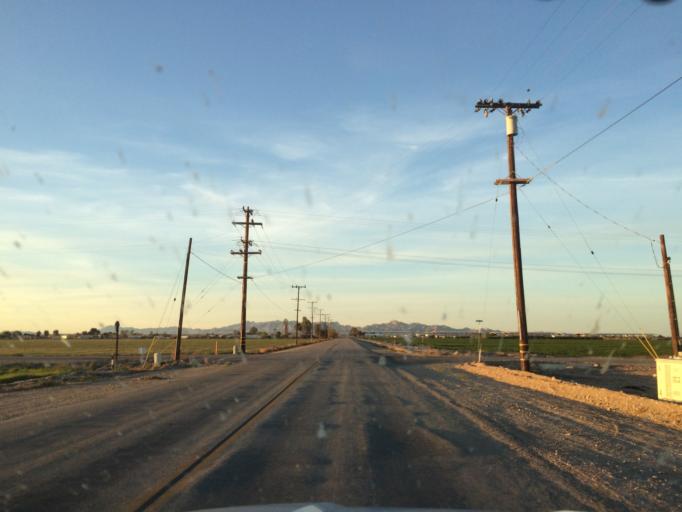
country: US
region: California
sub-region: Riverside County
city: Blythe
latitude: 33.5732
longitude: -114.6045
